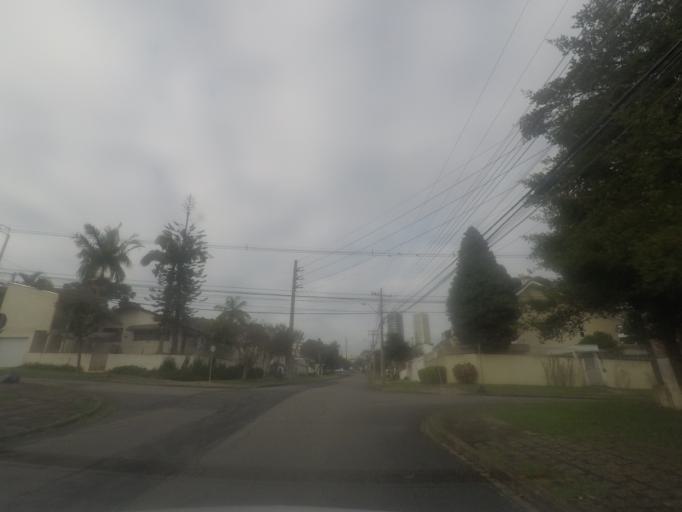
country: BR
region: Parana
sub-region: Curitiba
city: Curitiba
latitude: -25.4184
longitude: -49.2838
